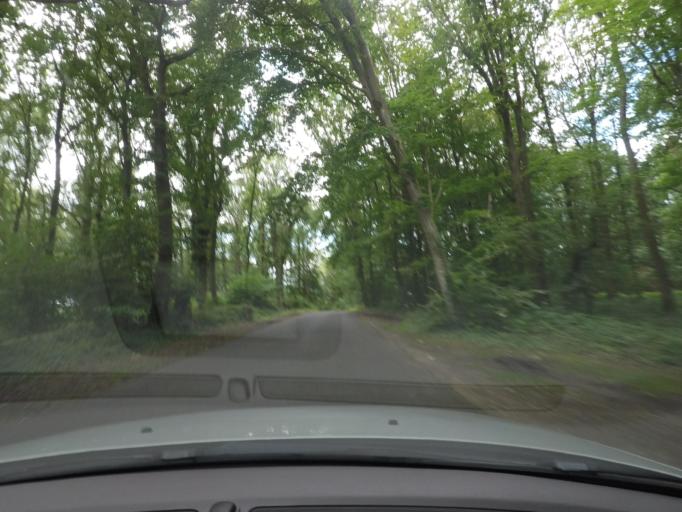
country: FR
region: Haute-Normandie
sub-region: Departement de l'Eure
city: Les Andelys
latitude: 49.2379
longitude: 1.4108
